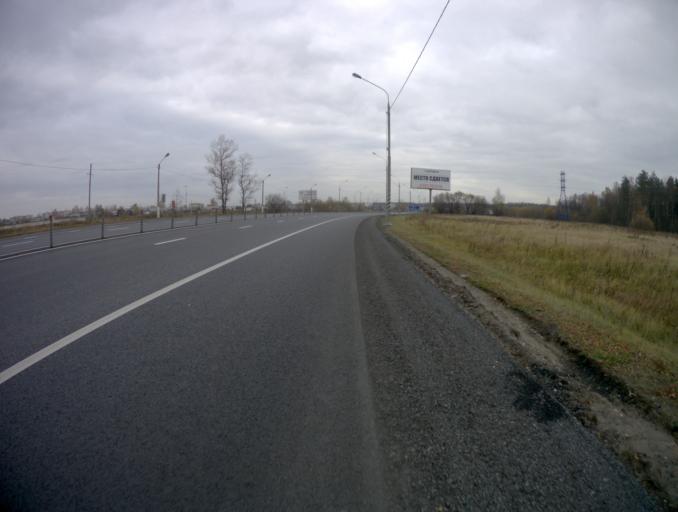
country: RU
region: Moskovskaya
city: Malaya Dubna
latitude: 55.8720
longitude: 38.9631
